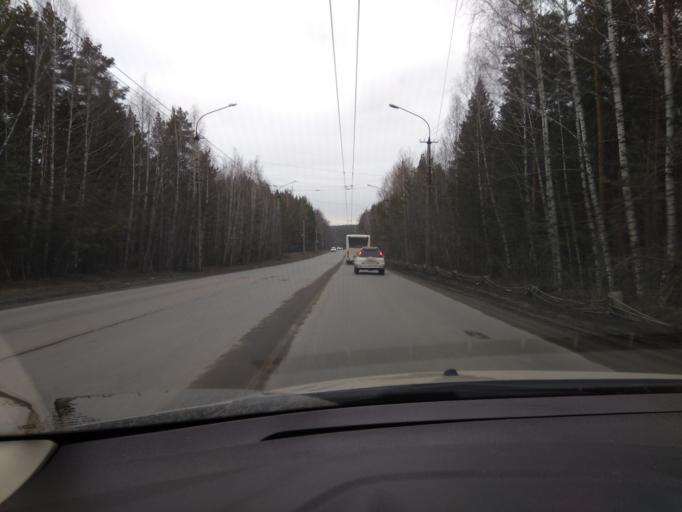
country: RU
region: Chelyabinsk
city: Turgoyak
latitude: 55.1224
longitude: 60.1320
